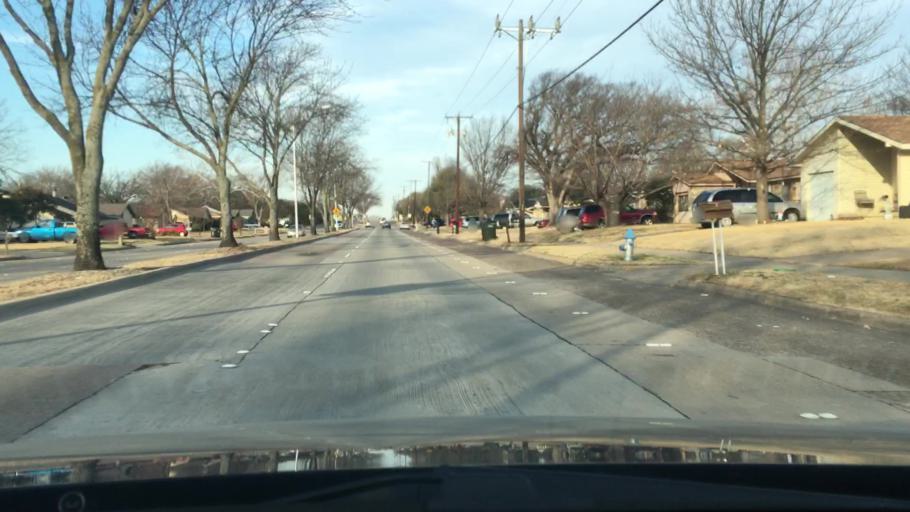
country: US
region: Texas
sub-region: Collin County
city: Plano
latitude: 33.0314
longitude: -96.6924
